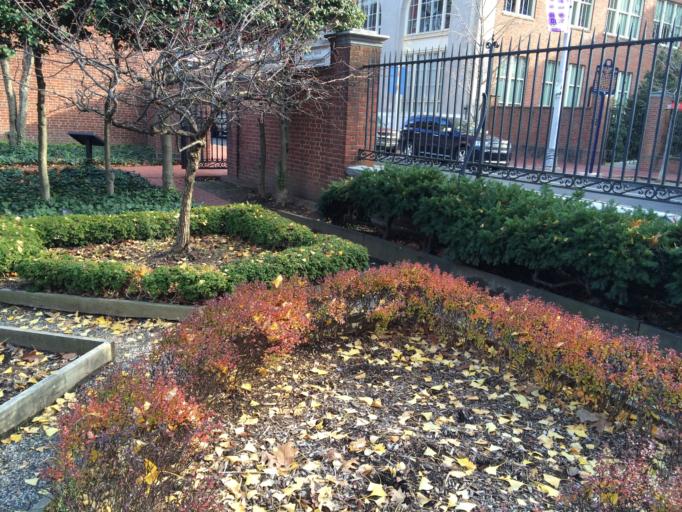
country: US
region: Pennsylvania
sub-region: Philadelphia County
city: Philadelphia
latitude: 39.9474
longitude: -75.1476
